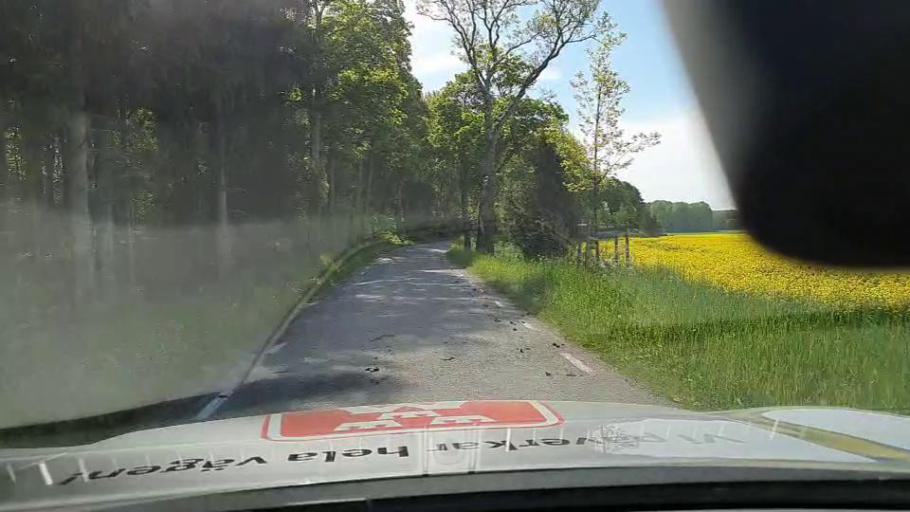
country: SE
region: Soedermanland
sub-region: Eskilstuna Kommun
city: Arla
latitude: 59.2589
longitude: 16.6721
